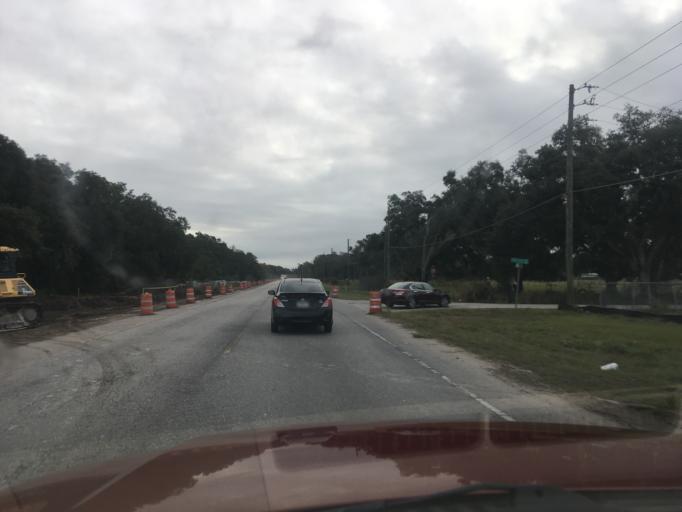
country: US
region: Florida
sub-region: Hillsborough County
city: Plant City
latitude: 28.0476
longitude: -82.1097
